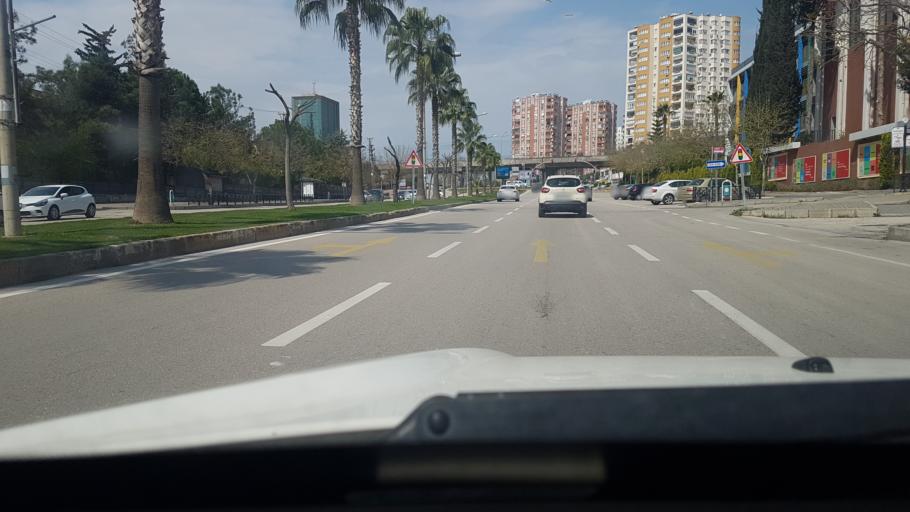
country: TR
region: Adana
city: Seyhan
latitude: 37.0476
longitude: 35.2716
